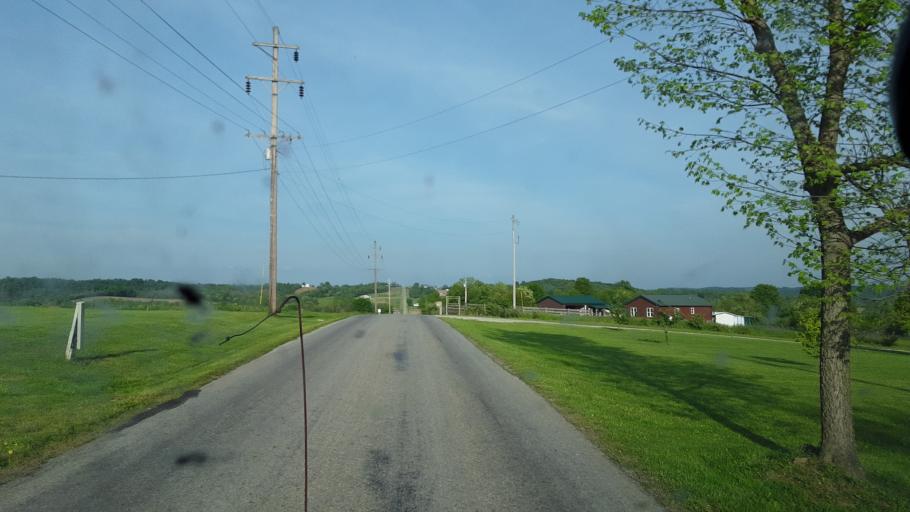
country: US
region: Ohio
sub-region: Ross County
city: Kingston
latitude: 39.5134
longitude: -82.7786
